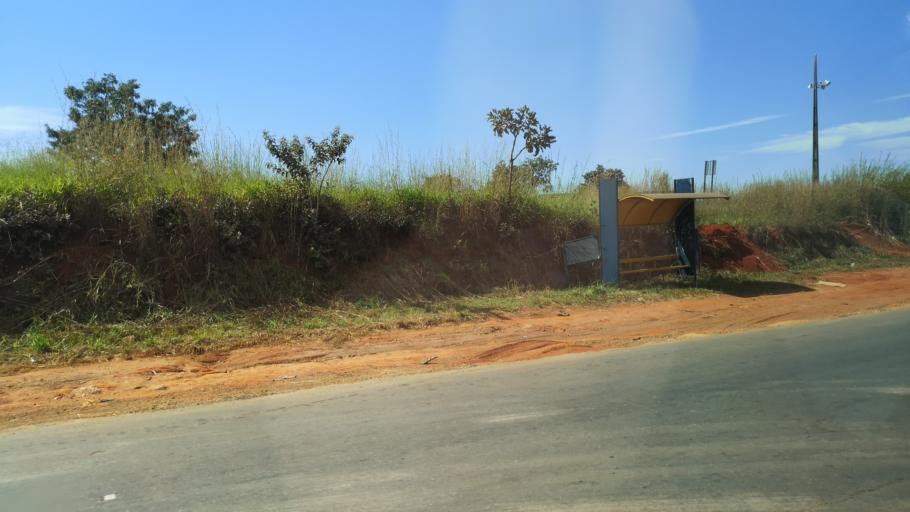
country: BR
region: Goias
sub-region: Senador Canedo
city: Senador Canedo
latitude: -16.7146
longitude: -49.1116
